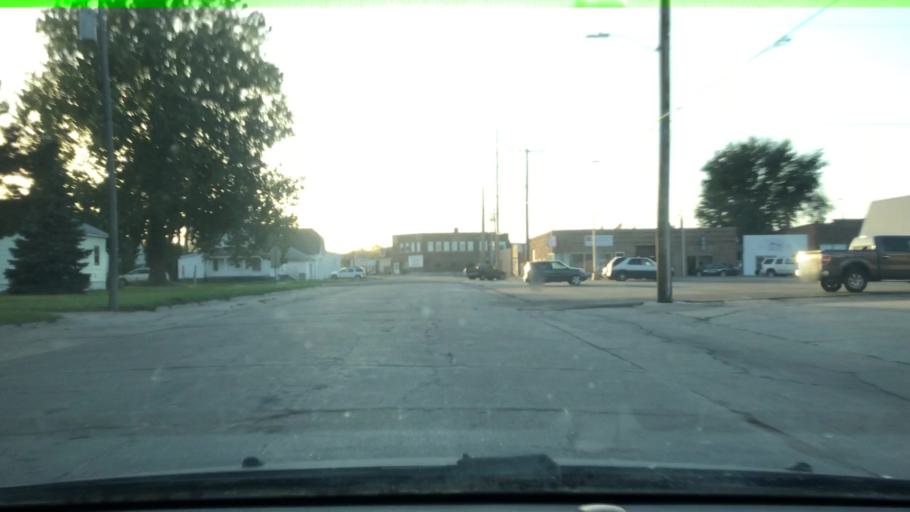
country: US
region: Nebraska
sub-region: Merrick County
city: Central City
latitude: 41.1151
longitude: -97.9994
